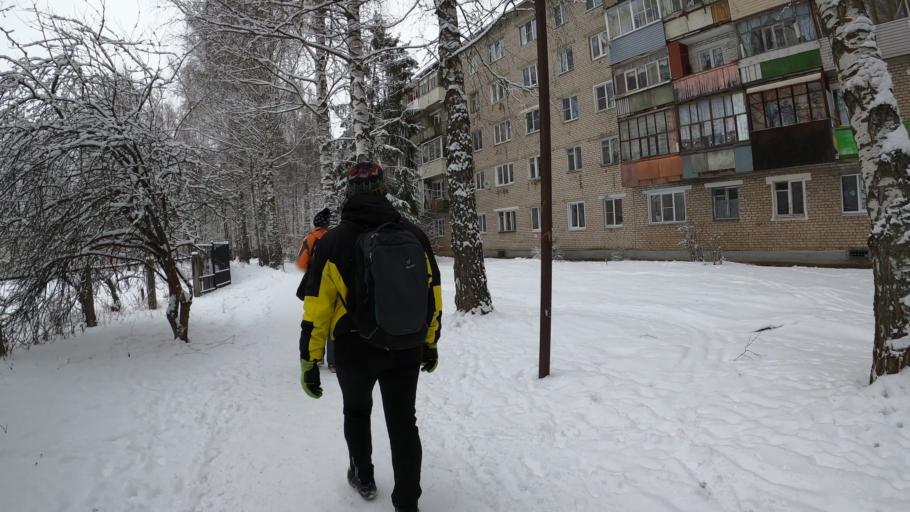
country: RU
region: Jaroslavl
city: Pereslavl'-Zalesskiy
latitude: 56.7542
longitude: 38.8711
